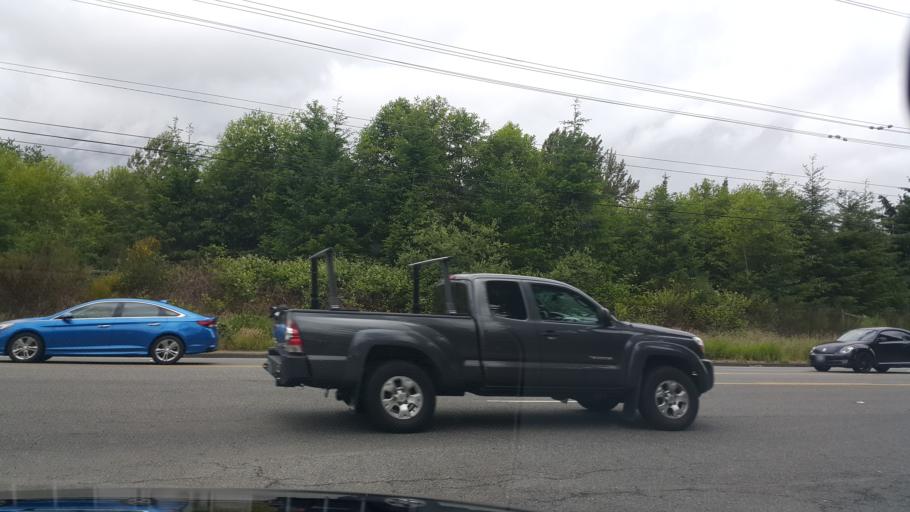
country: US
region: Washington
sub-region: King County
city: Fairwood
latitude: 47.4402
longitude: -122.1542
